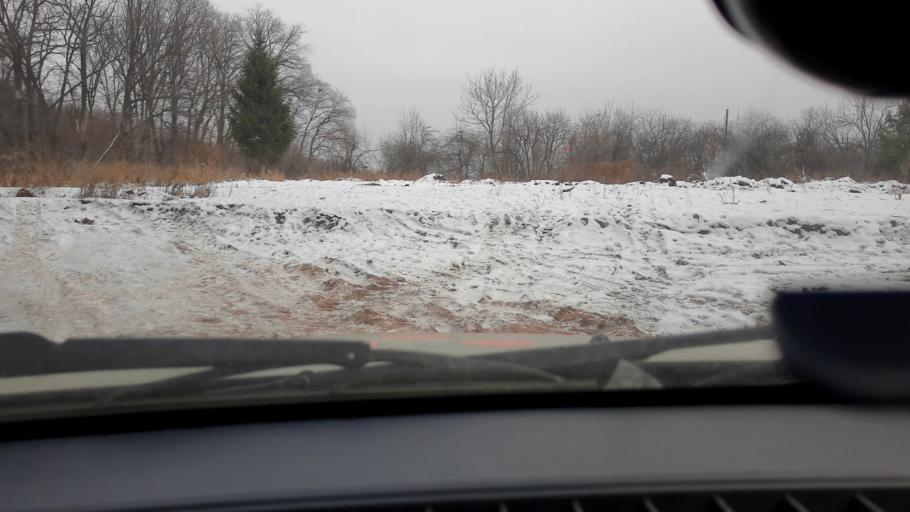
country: RU
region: Bashkortostan
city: Ufa
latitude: 54.7645
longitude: 56.0361
